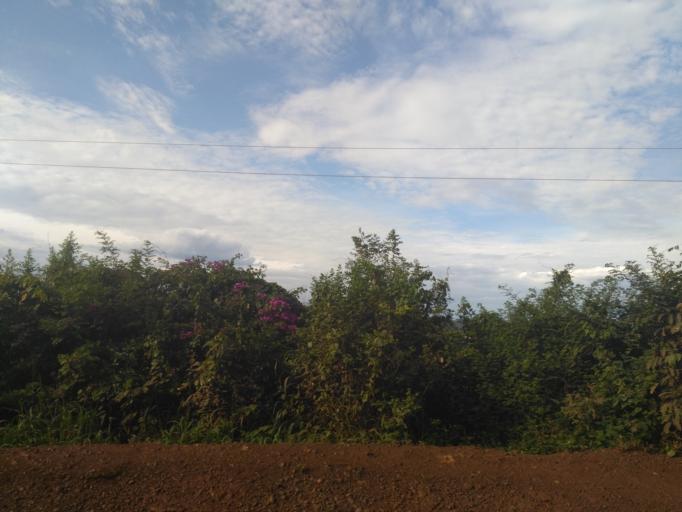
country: UG
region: Eastern Region
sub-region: Jinja District
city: Jinja
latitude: 0.4672
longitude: 33.1745
